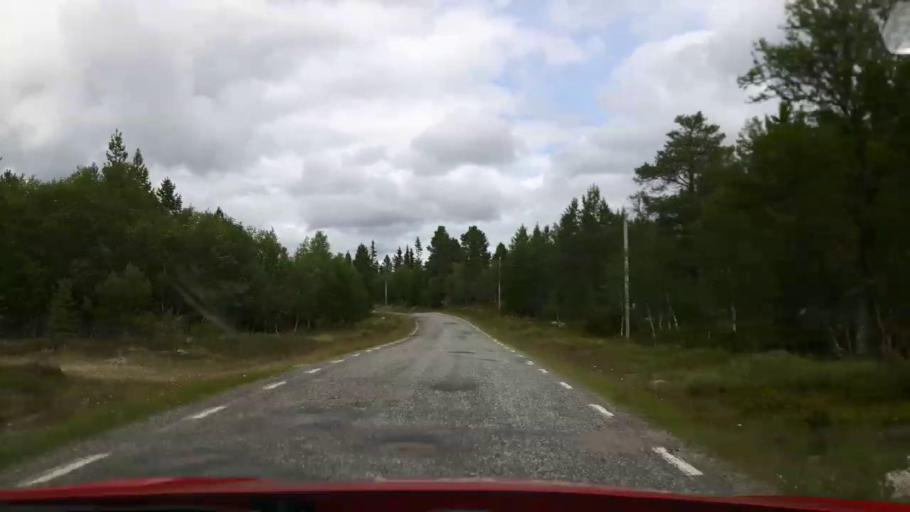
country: NO
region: Hedmark
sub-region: Engerdal
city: Engerdal
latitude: 62.3107
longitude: 12.8097
